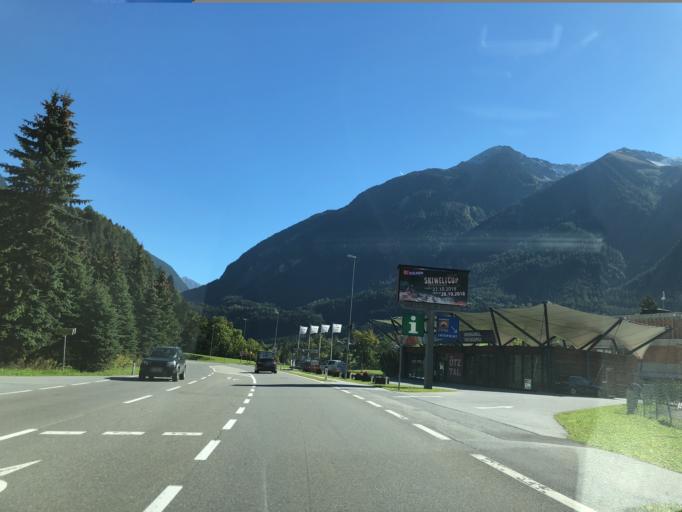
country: AT
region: Tyrol
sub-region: Politischer Bezirk Imst
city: Sautens
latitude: 47.2154
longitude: 10.8667
